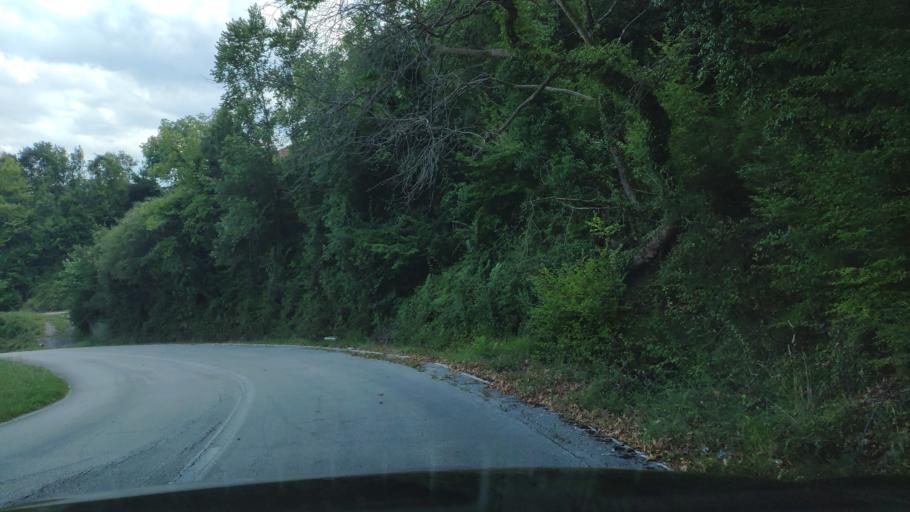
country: GR
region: Epirus
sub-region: Nomos Artas
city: Agios Dimitrios
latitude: 39.4577
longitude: 21.0288
